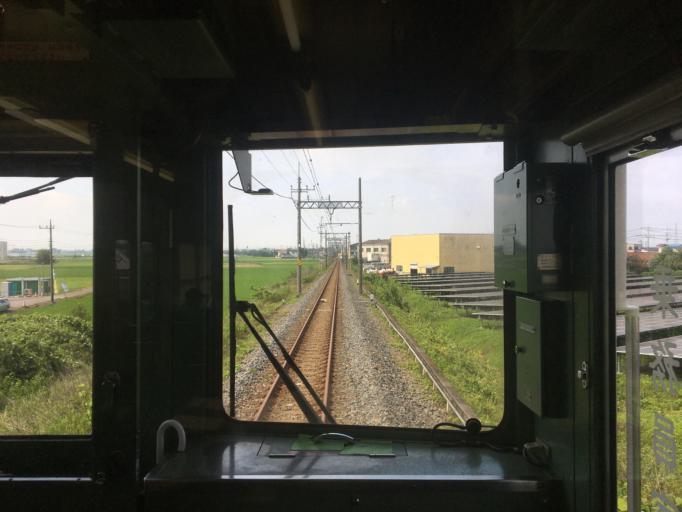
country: JP
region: Tochigi
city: Sano
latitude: 36.2955
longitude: 139.5689
